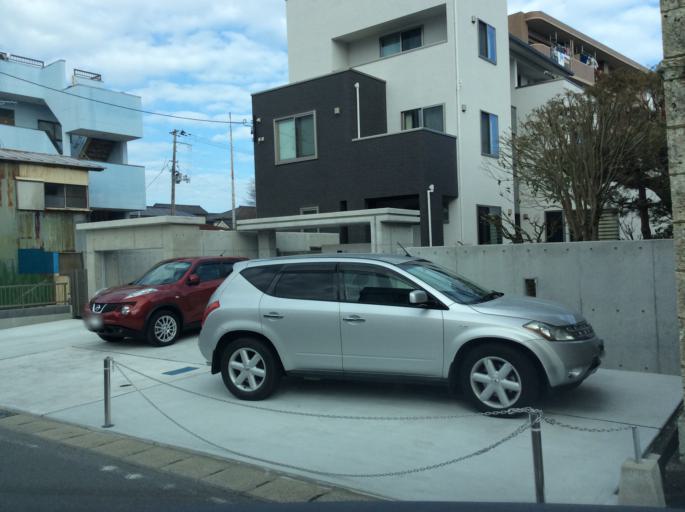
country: JP
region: Fukushima
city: Iwaki
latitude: 36.9504
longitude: 140.9059
